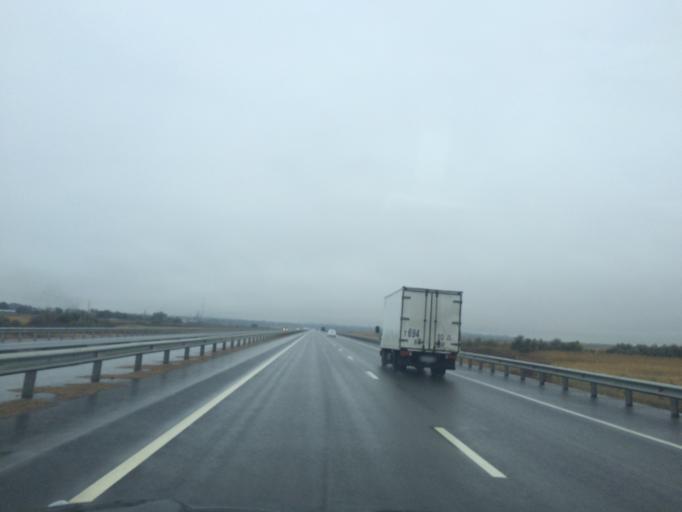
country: RU
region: Rostov
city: Kuleshovka
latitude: 47.0889
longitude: 39.5233
